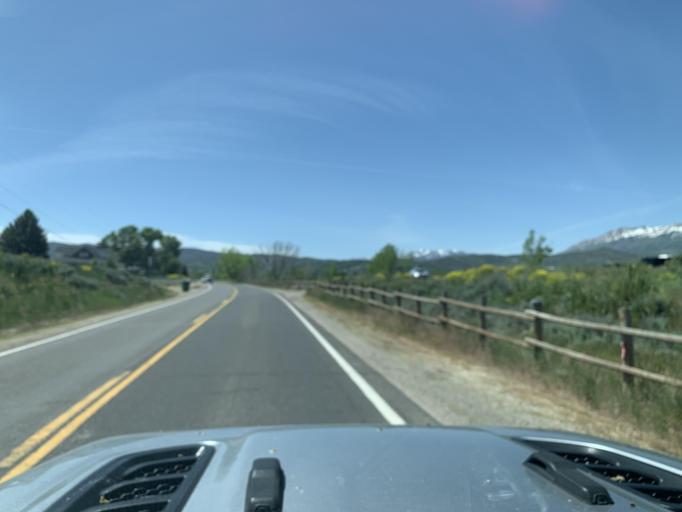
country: US
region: Utah
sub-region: Weber County
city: Wolf Creek
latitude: 41.2729
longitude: -111.7772
